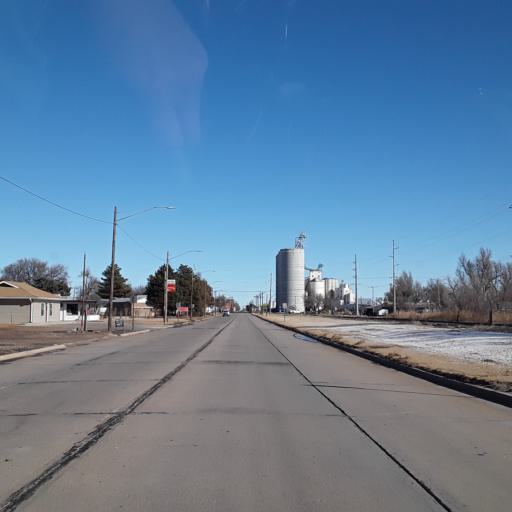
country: US
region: Kansas
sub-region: Pawnee County
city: Larned
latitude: 38.1726
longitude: -99.1039
